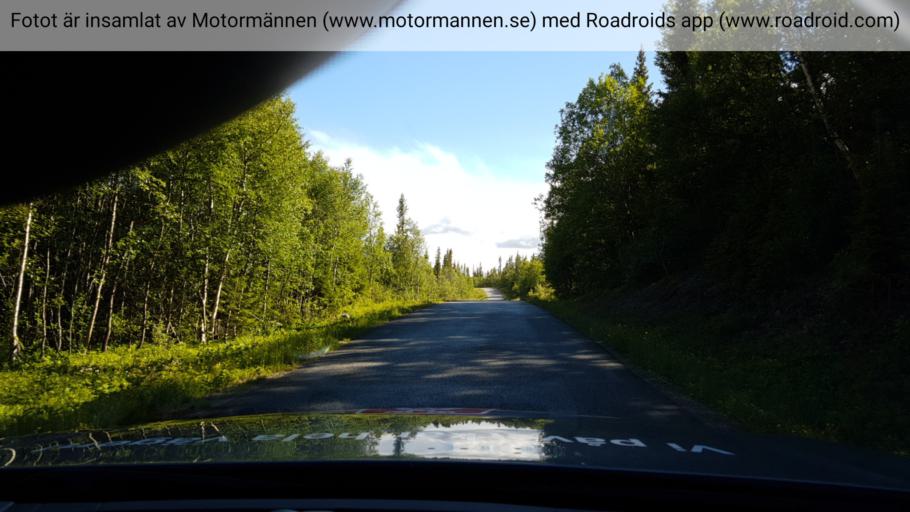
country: SE
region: Jaemtland
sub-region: Bergs Kommun
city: Hoverberg
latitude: 63.0140
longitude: 13.9423
